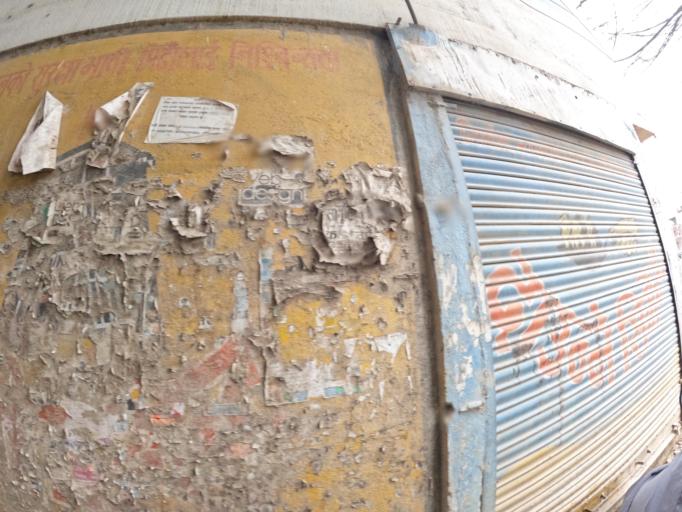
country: NP
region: Central Region
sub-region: Bagmati Zone
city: Kathmandu
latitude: 27.7354
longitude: 85.3139
